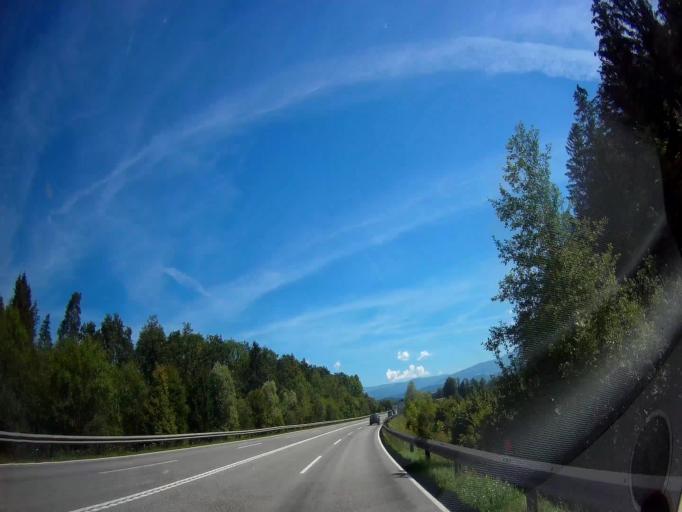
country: AT
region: Carinthia
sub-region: Politischer Bezirk Sankt Veit an der Glan
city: Molbling
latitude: 46.8184
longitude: 14.4327
